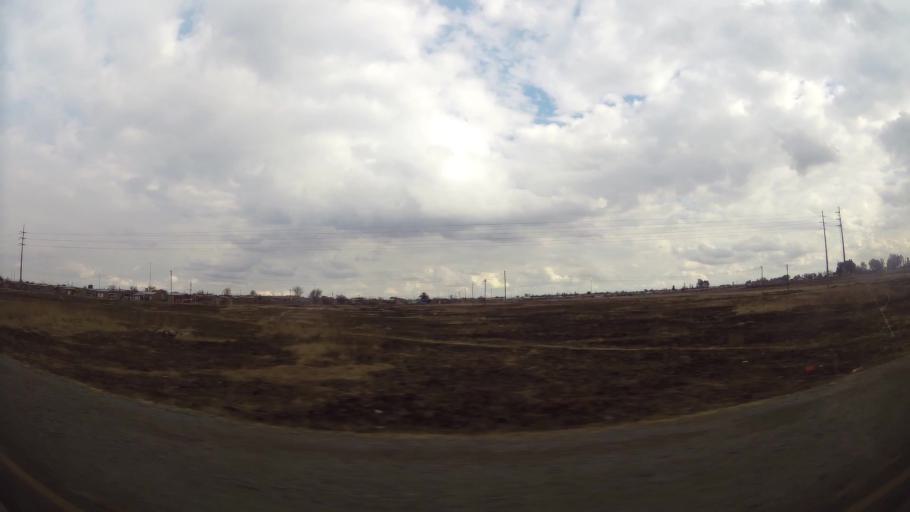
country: ZA
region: Orange Free State
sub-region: Fezile Dabi District Municipality
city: Sasolburg
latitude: -26.8438
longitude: 27.8835
